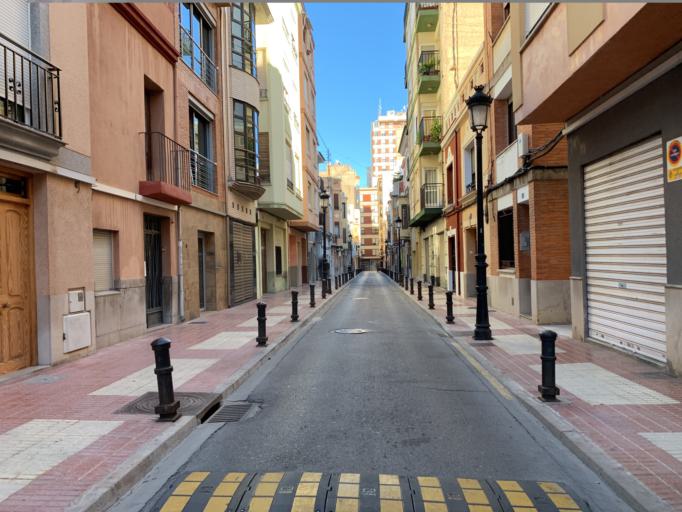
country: ES
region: Valencia
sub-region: Provincia de Castello
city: Castello de la Plana
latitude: 39.9852
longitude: -0.0426
